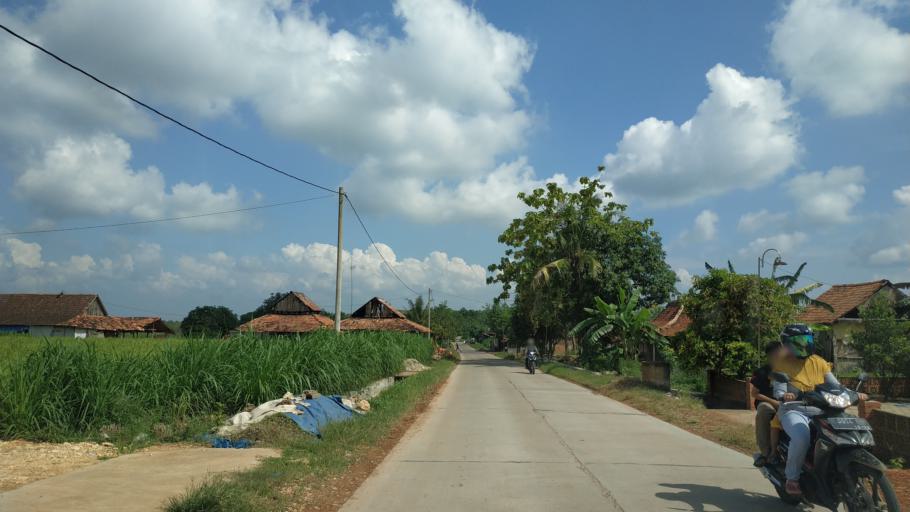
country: ID
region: Central Java
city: Jepang
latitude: -7.0134
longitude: 111.1171
